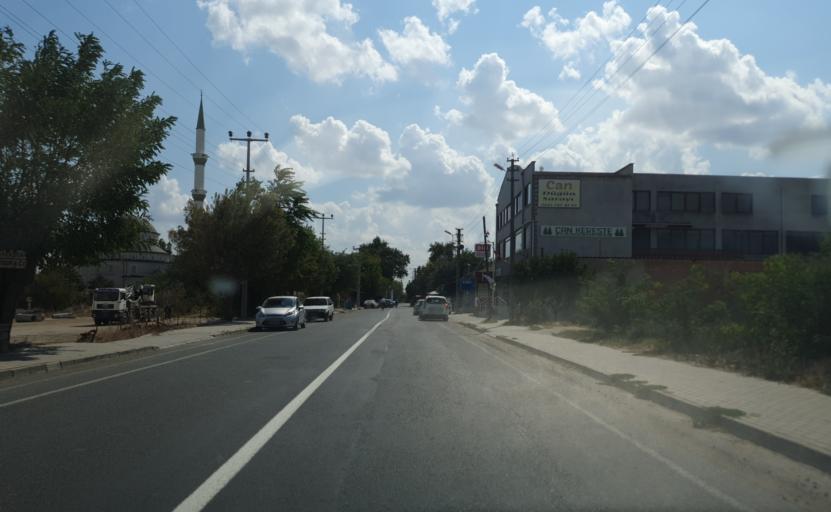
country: TR
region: Kirklareli
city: Luleburgaz
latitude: 41.3582
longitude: 27.3351
